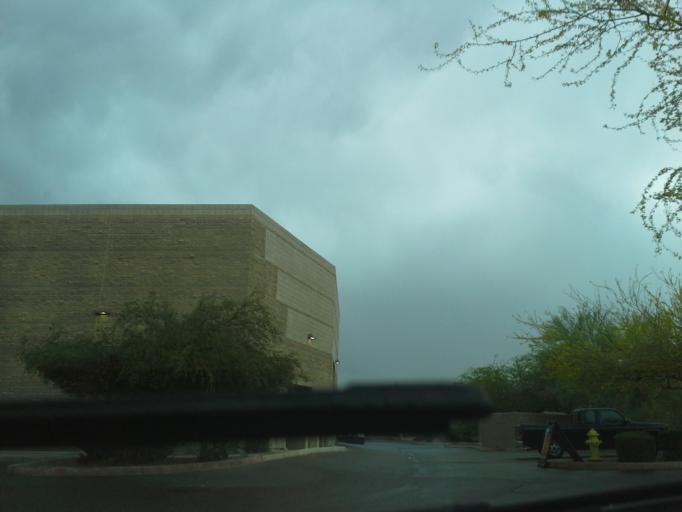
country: US
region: Arizona
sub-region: Maricopa County
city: Paradise Valley
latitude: 33.6379
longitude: -111.8864
